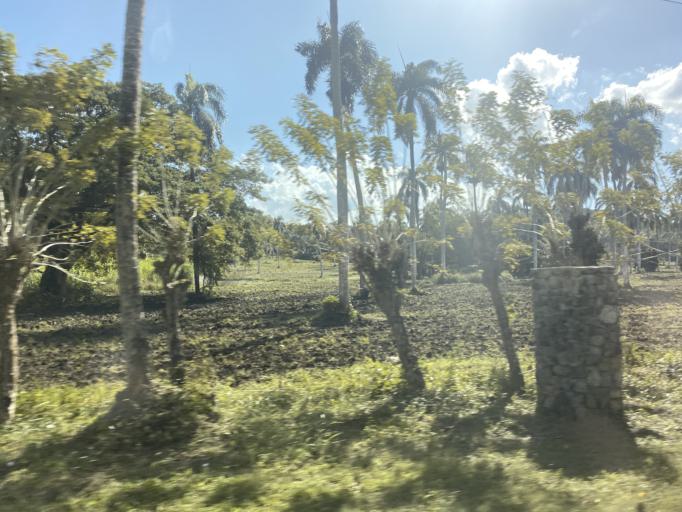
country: DO
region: Maria Trinidad Sanchez
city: Rio San Juan
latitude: 19.6152
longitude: -70.1311
